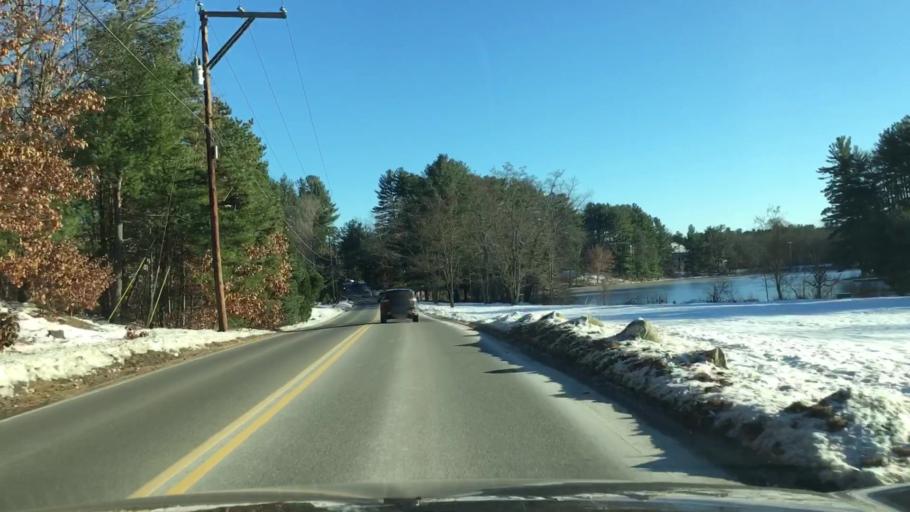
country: US
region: New Hampshire
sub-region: Hillsborough County
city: Hollis
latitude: 42.8085
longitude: -71.5589
